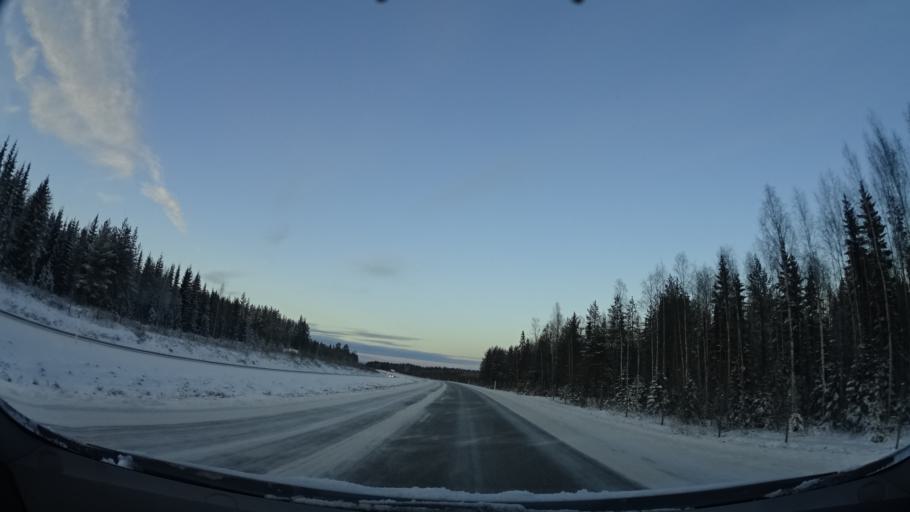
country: SE
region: Vaesterbotten
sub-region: Skelleftea Kommun
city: Kage
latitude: 64.8066
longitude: 21.0331
